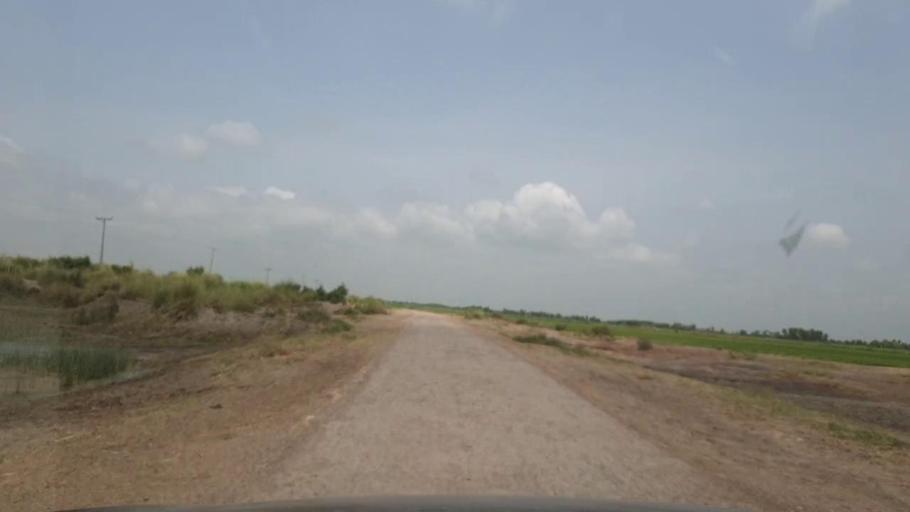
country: PK
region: Sindh
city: Ratodero
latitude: 27.9127
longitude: 68.3003
